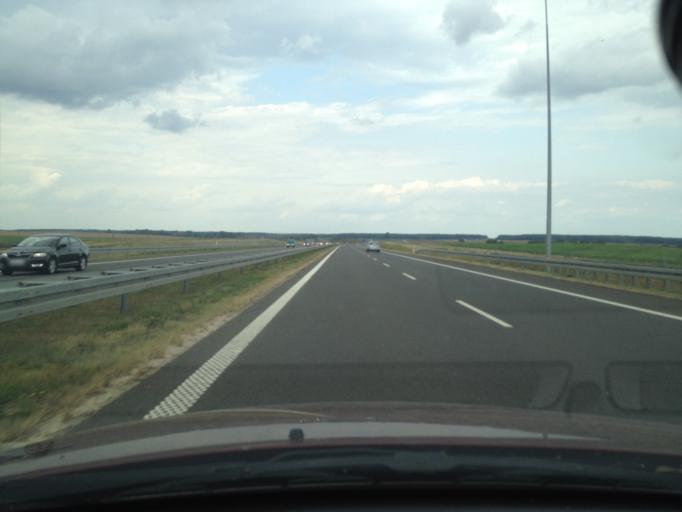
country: PL
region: West Pomeranian Voivodeship
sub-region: Powiat pyrzycki
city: Bielice
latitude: 53.1288
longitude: 14.7317
